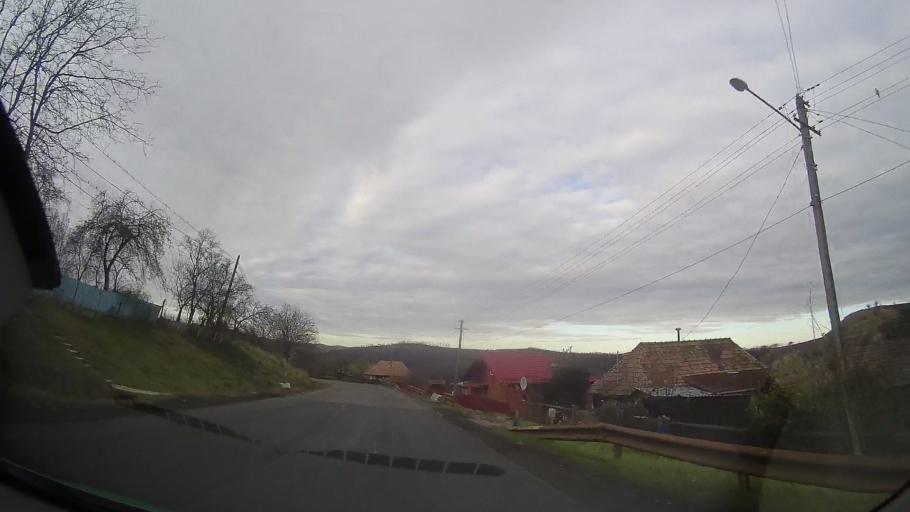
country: RO
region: Bistrita-Nasaud
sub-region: Comuna Silvasu de Campie
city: Silvasu de Campie
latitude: 46.7785
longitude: 24.3054
